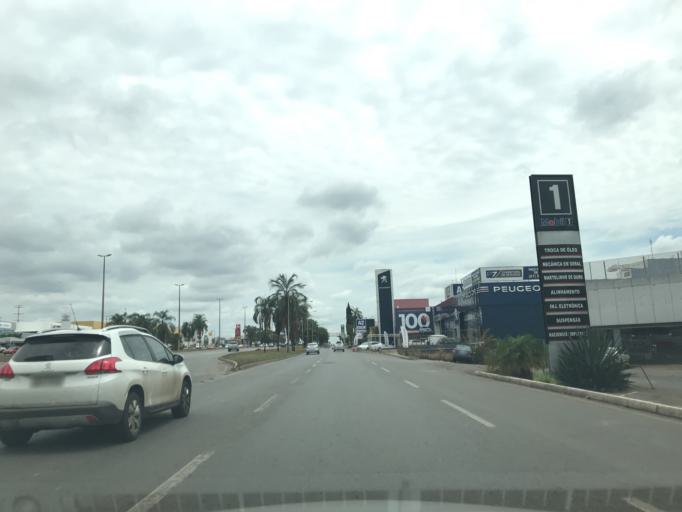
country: BR
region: Federal District
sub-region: Brasilia
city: Brasilia
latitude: -15.8568
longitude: -47.9556
